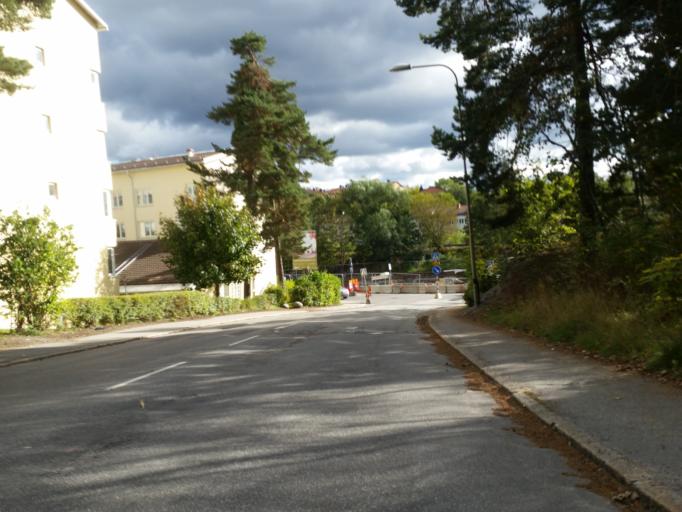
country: SE
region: Stockholm
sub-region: Stockholms Kommun
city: OEstermalm
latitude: 59.2957
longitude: 18.0965
